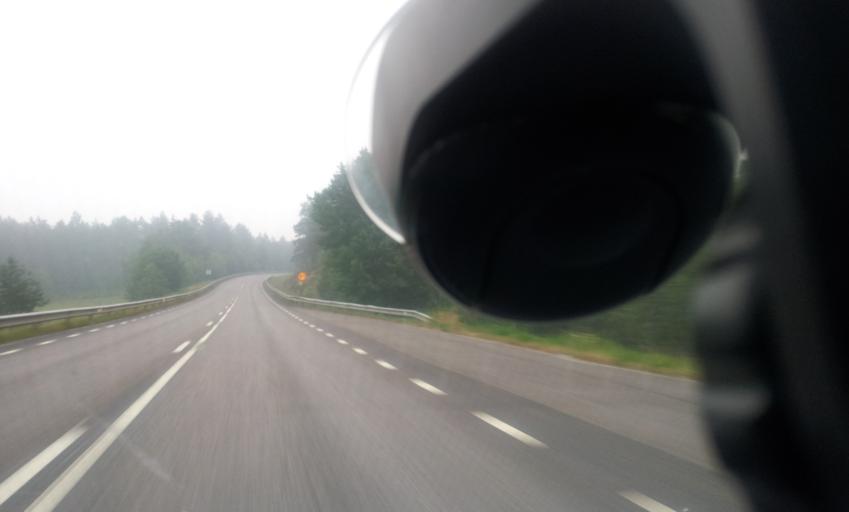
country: SE
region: Kalmar
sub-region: Vasterviks Kommun
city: Ankarsrum
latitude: 57.7224
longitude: 16.4772
